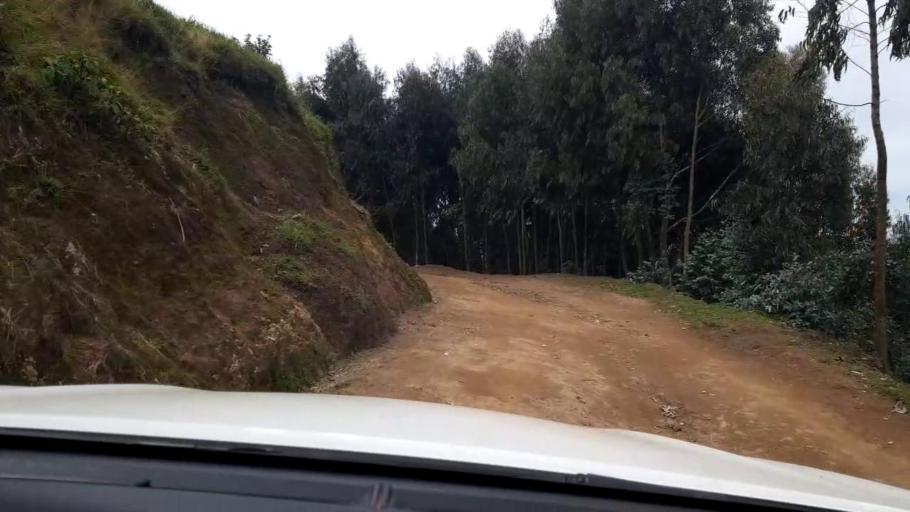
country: RW
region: Western Province
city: Kibuye
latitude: -1.8829
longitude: 29.4541
